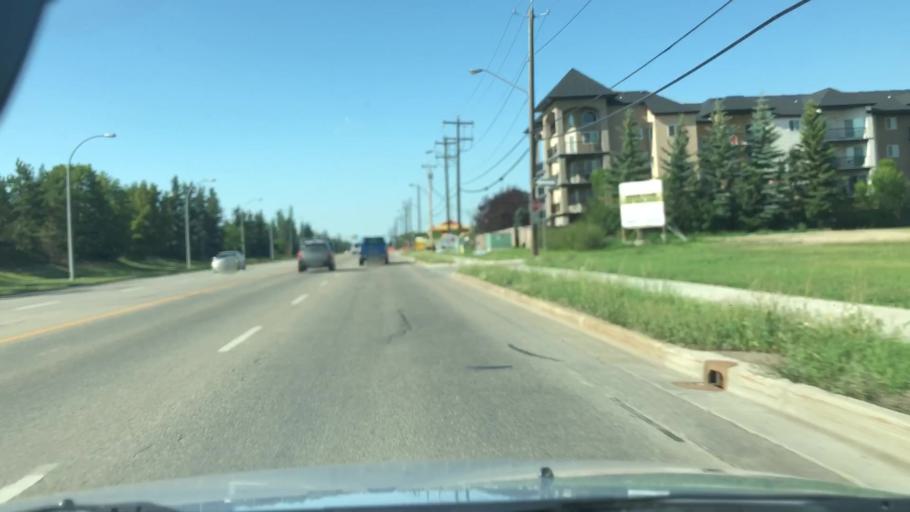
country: CA
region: Alberta
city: Edmonton
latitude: 53.6076
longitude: -113.5412
